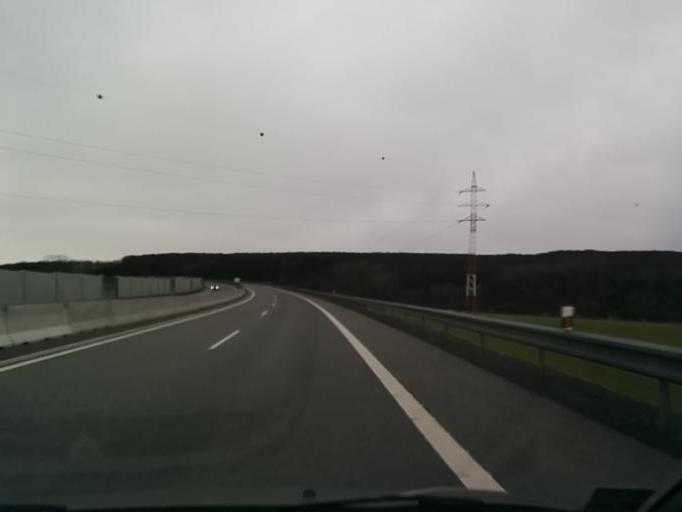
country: SK
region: Nitriansky
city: Zlate Moravce
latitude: 48.3517
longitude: 18.4704
